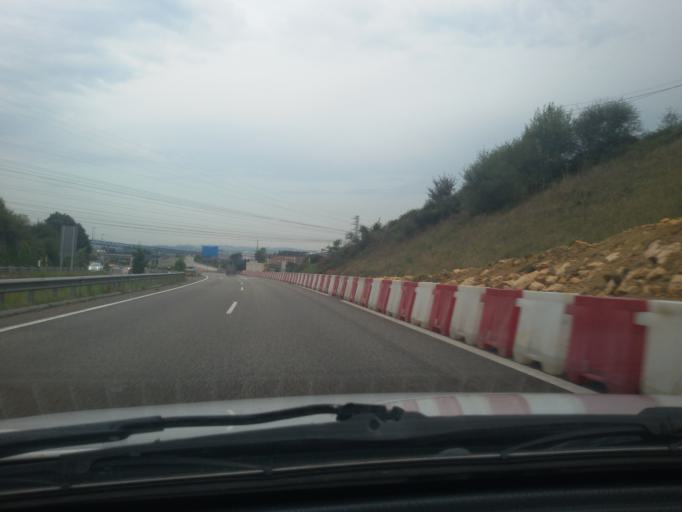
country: ES
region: Asturias
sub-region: Province of Asturias
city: Oviedo
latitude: 43.3821
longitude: -5.8321
